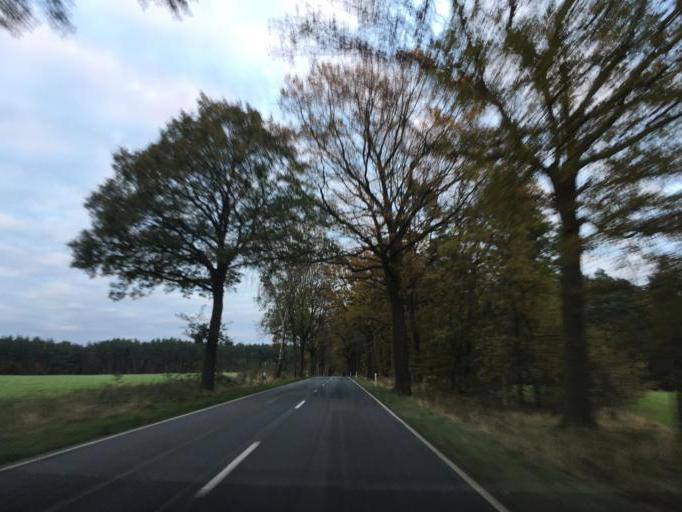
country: DE
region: Lower Saxony
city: Rullstorf
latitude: 53.2591
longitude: 10.5405
